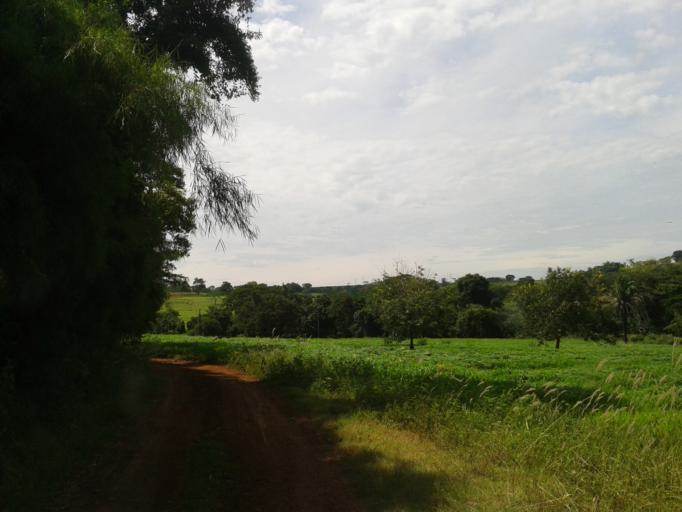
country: BR
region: Minas Gerais
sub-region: Centralina
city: Centralina
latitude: -18.6915
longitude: -49.2099
